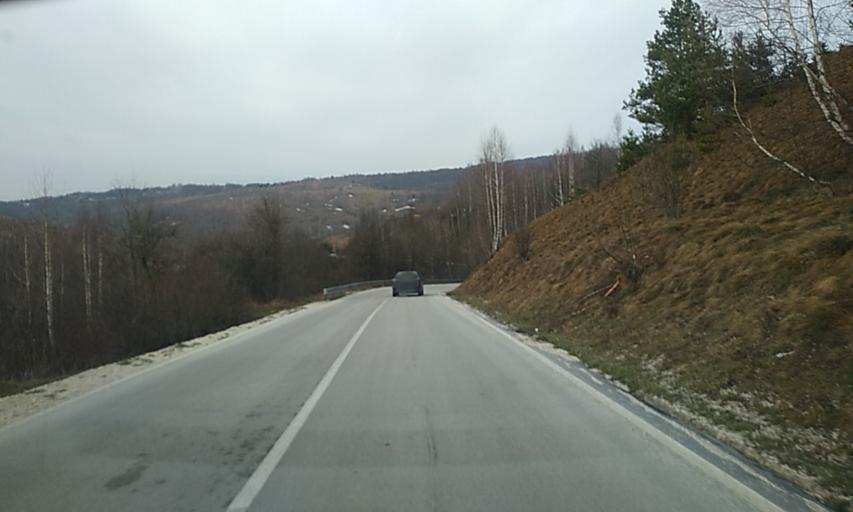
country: RS
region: Central Serbia
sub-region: Pcinjski Okrug
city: Bosilegrad
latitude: 42.6484
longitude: 22.3835
